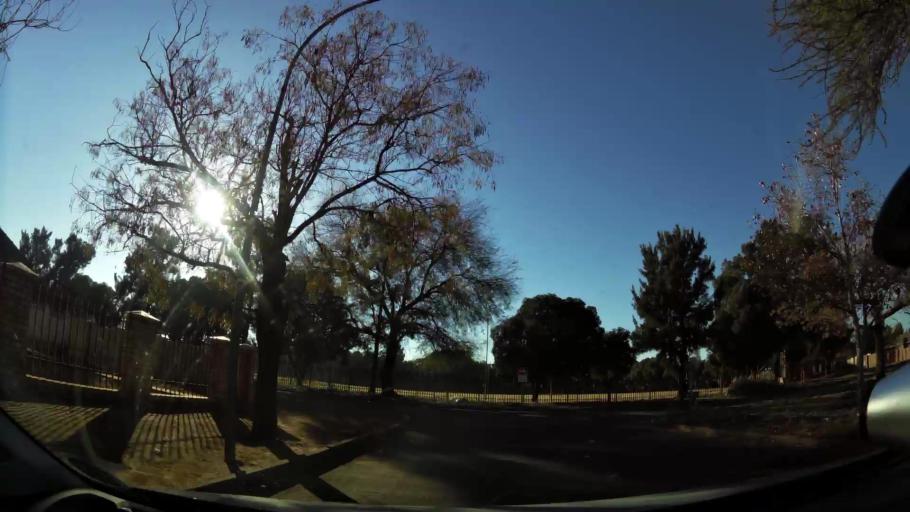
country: ZA
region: Northern Cape
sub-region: Frances Baard District Municipality
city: Kimberley
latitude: -28.7388
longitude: 24.7352
